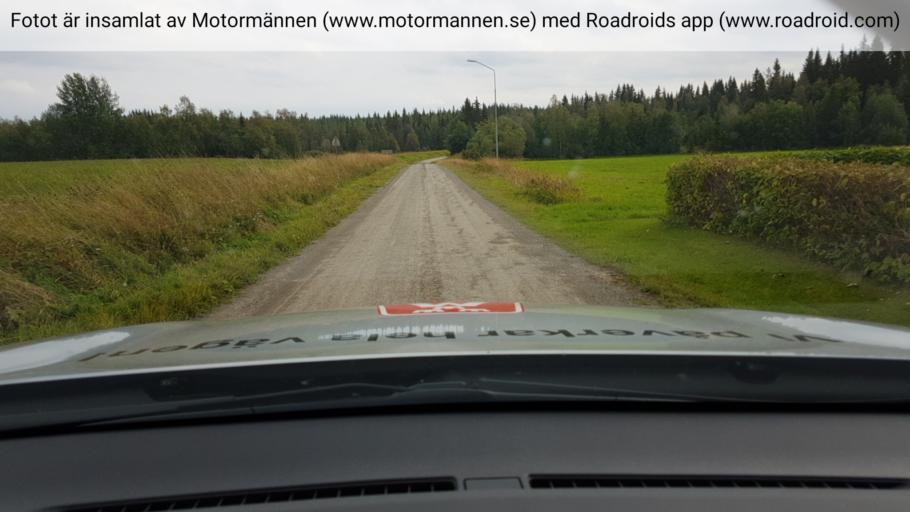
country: SE
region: Jaemtland
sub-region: Stroemsunds Kommun
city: Stroemsund
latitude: 63.7642
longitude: 15.3449
